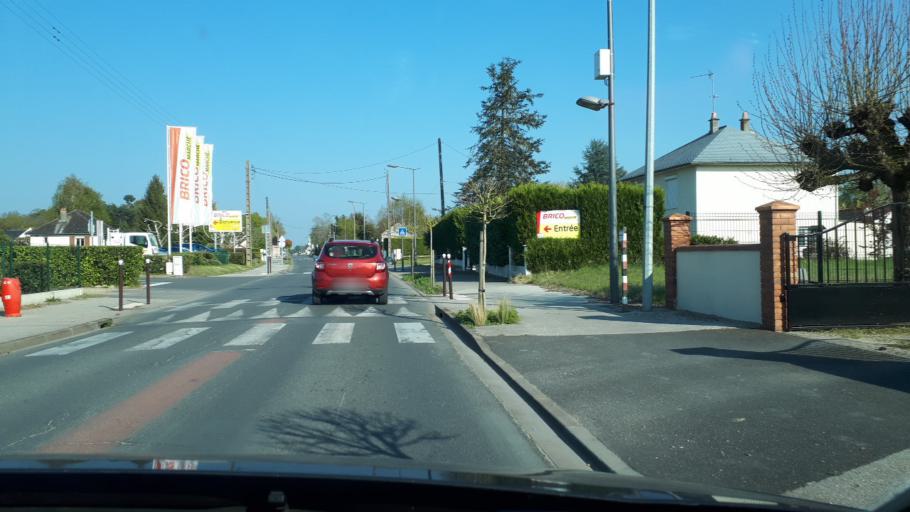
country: FR
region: Centre
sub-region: Departement d'Indre-et-Loire
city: Blere
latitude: 47.3248
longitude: 1.0074
